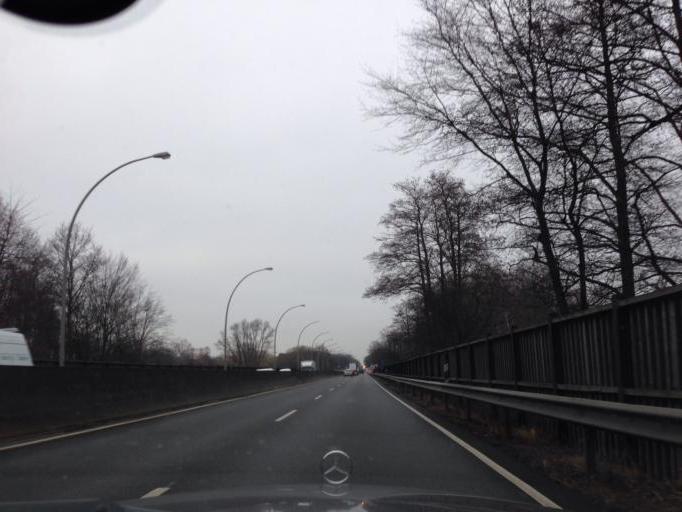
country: DE
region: Hamburg
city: Harburg
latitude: 53.4926
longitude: 9.9972
